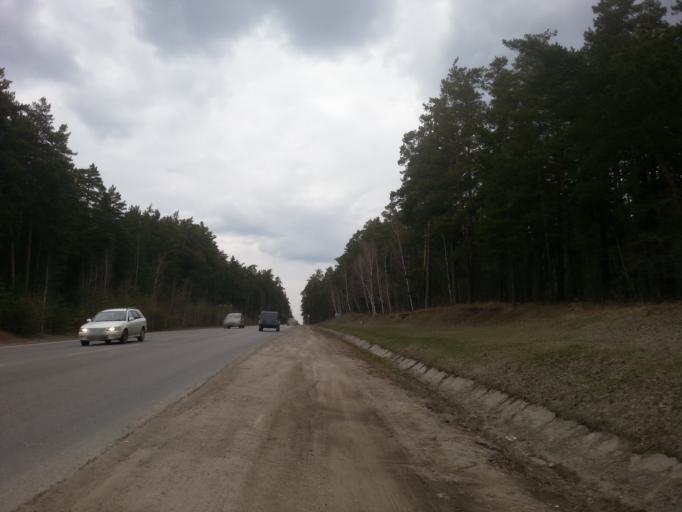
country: RU
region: Altai Krai
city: Yuzhnyy
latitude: 53.2696
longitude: 83.7255
